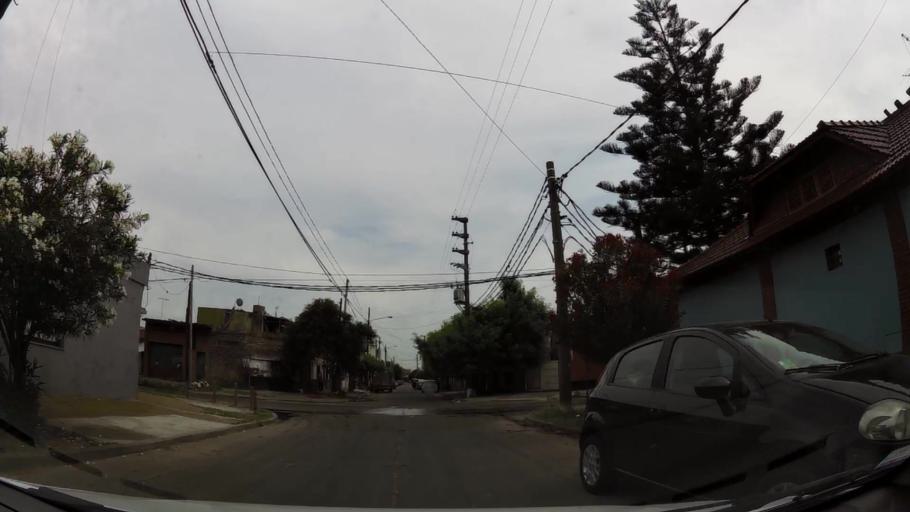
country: AR
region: Buenos Aires
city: San Justo
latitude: -34.6890
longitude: -58.5184
